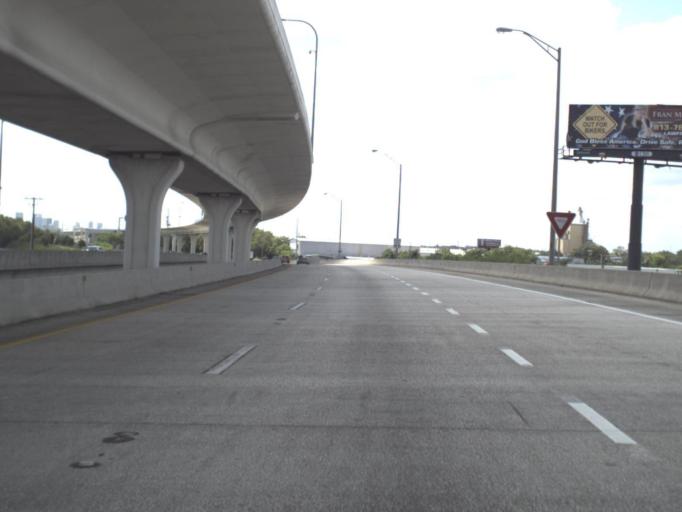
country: US
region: Florida
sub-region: Hillsborough County
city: Palm River-Clair Mel
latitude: 27.9502
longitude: -82.3695
